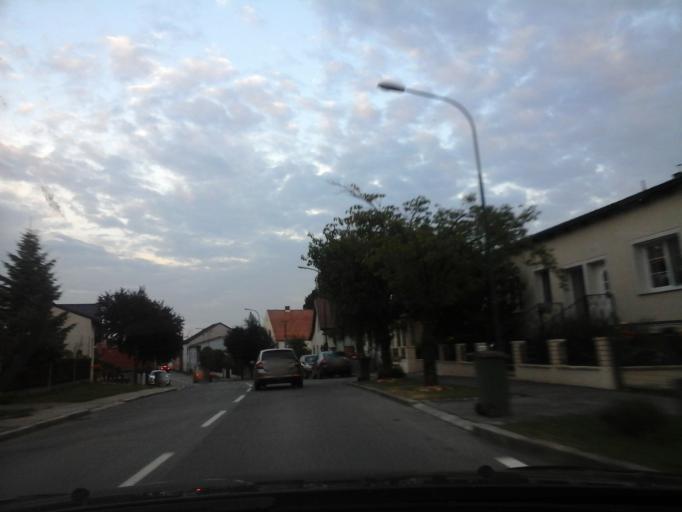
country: AT
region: Lower Austria
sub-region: Politischer Bezirk Bruck an der Leitha
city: Scharndorf
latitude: 48.0964
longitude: 16.7942
